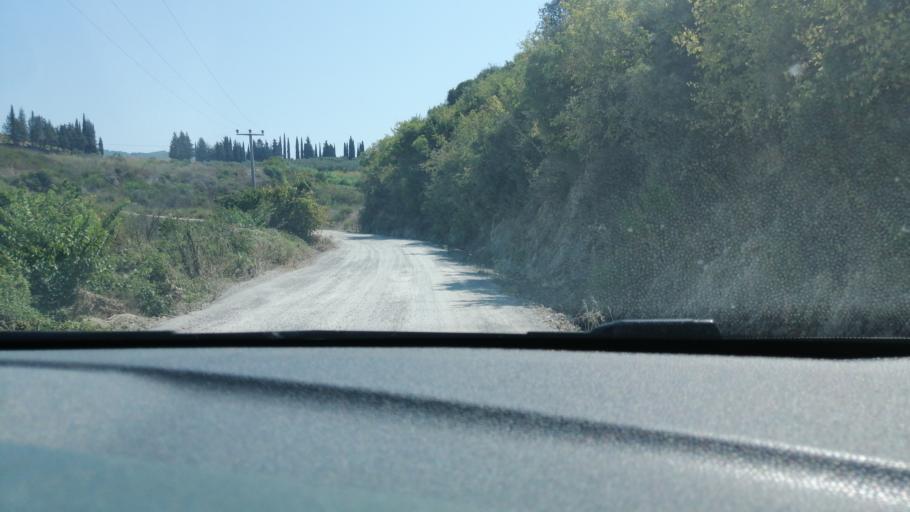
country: TR
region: Aydin
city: Davutlar
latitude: 37.7834
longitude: 27.3148
